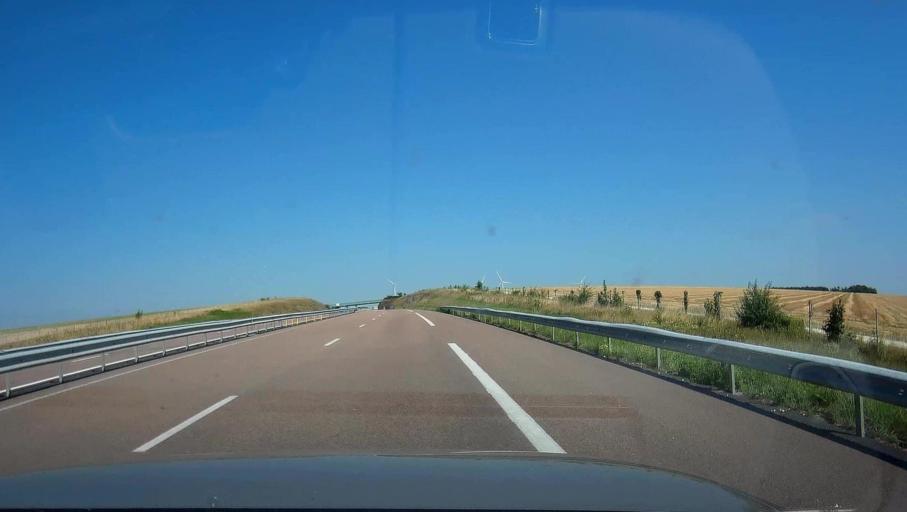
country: FR
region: Champagne-Ardenne
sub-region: Departement de l'Aube
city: Arcis-sur-Aube
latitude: 48.4382
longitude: 4.1554
